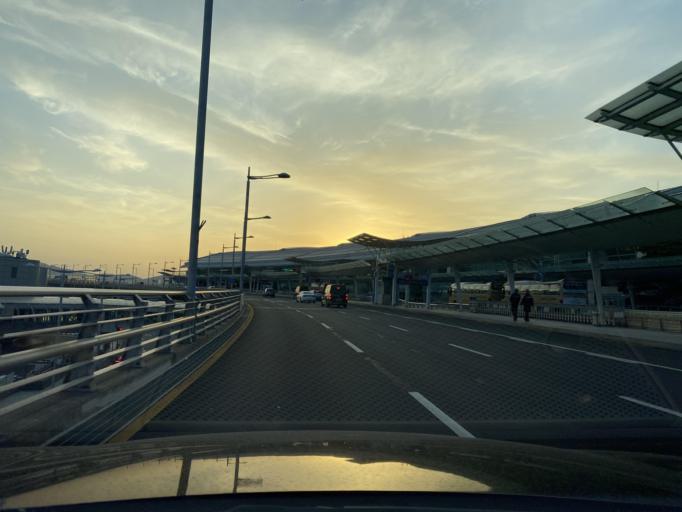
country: KR
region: Incheon
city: Incheon
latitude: 37.4488
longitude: 126.4519
